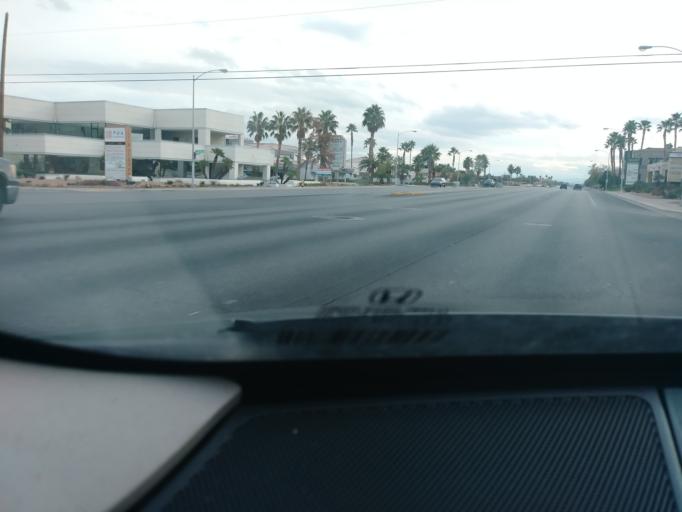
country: US
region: Nevada
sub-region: Clark County
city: Spring Valley
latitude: 36.1425
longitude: -115.2431
